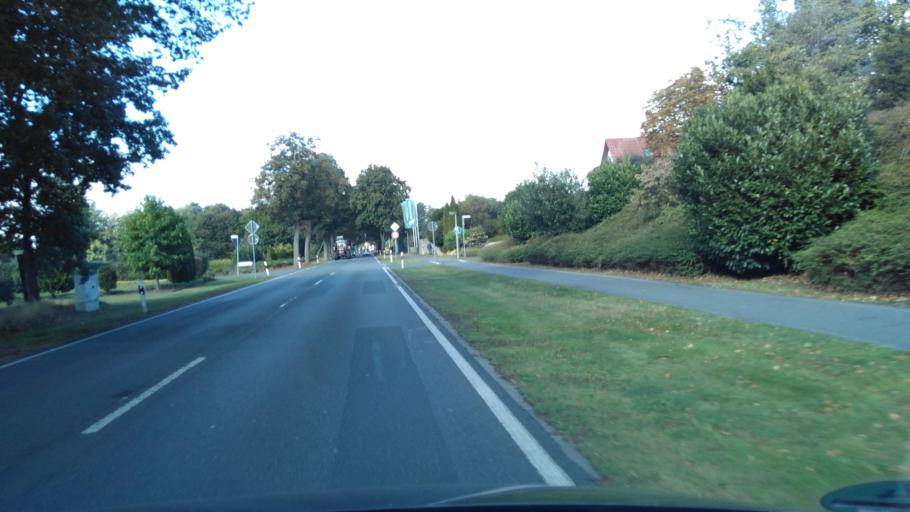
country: DE
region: North Rhine-Westphalia
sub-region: Regierungsbezirk Detmold
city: Verl
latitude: 51.8760
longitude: 8.5304
